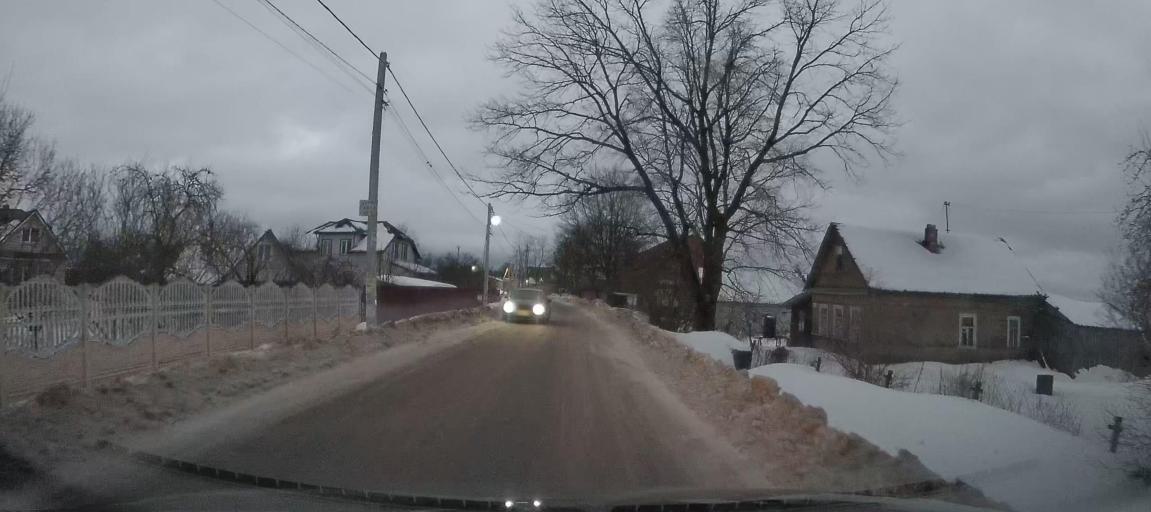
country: RU
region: Leningrad
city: Taytsy
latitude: 59.6980
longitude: 30.1391
